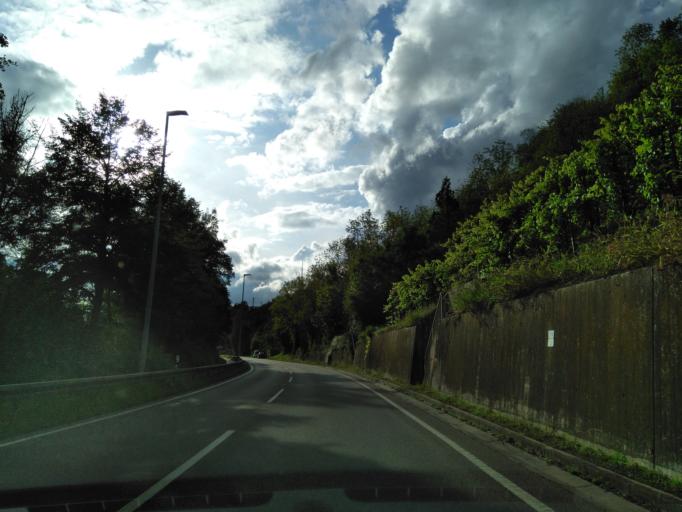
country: DE
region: Baden-Wuerttemberg
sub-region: Regierungsbezirk Stuttgart
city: Bietigheim-Bissingen
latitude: 48.9497
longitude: 9.0967
